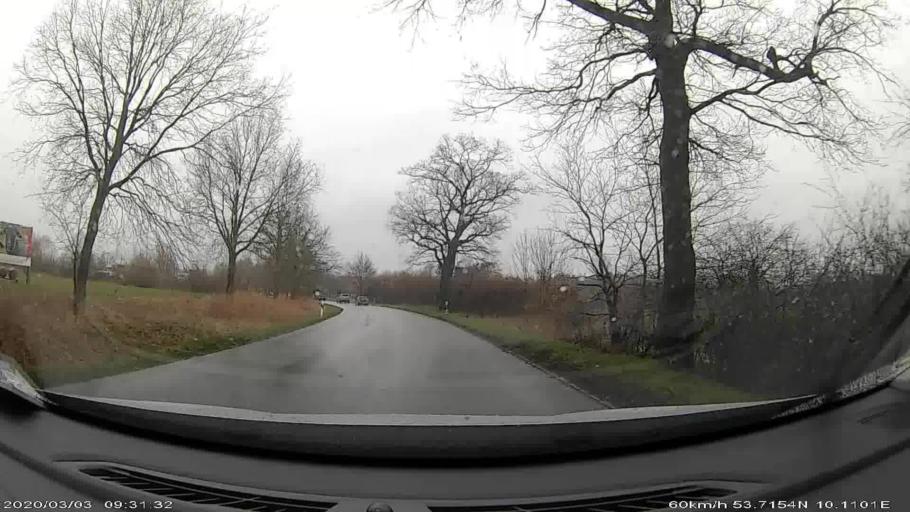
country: DE
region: Hamburg
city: Duvenstedt
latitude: 53.7187
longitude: 10.1110
